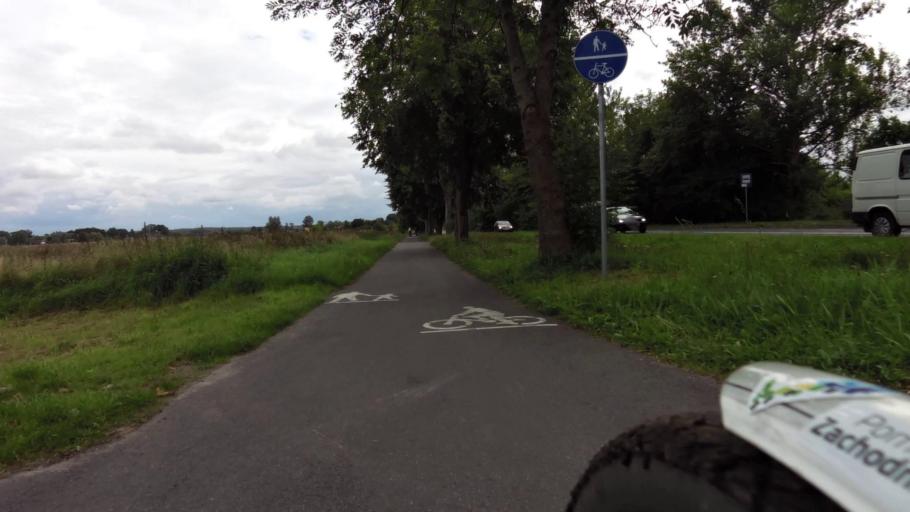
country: PL
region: West Pomeranian Voivodeship
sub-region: Powiat koszalinski
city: Mielno
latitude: 54.2461
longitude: 16.0641
